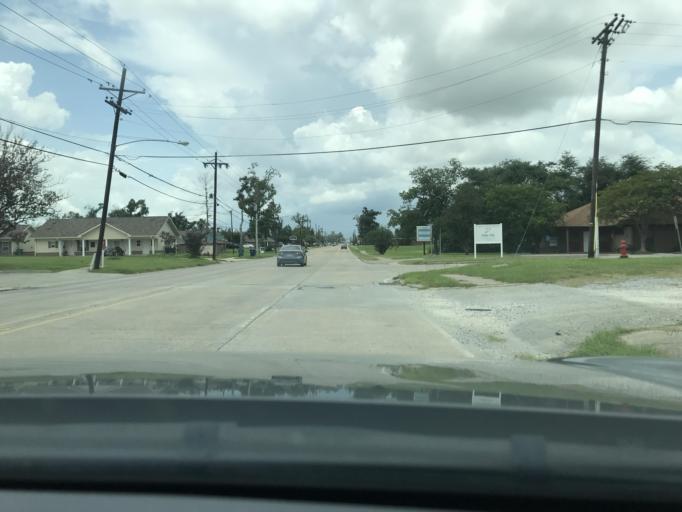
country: US
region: Louisiana
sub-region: Calcasieu Parish
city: Sulphur
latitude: 30.2277
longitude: -93.3283
